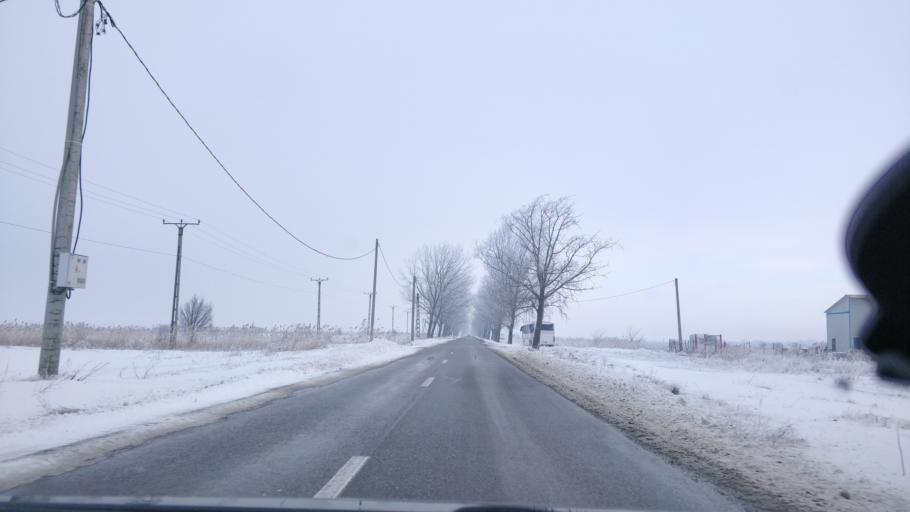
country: RO
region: Vrancea
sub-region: Comuna Vanatori
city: Jorasti
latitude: 45.6977
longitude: 27.2350
